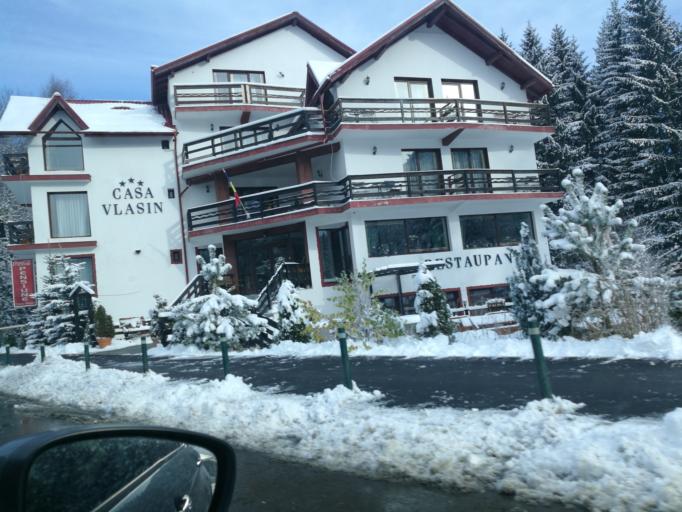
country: RO
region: Brasov
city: Brasov
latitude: 45.5960
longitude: 25.5532
